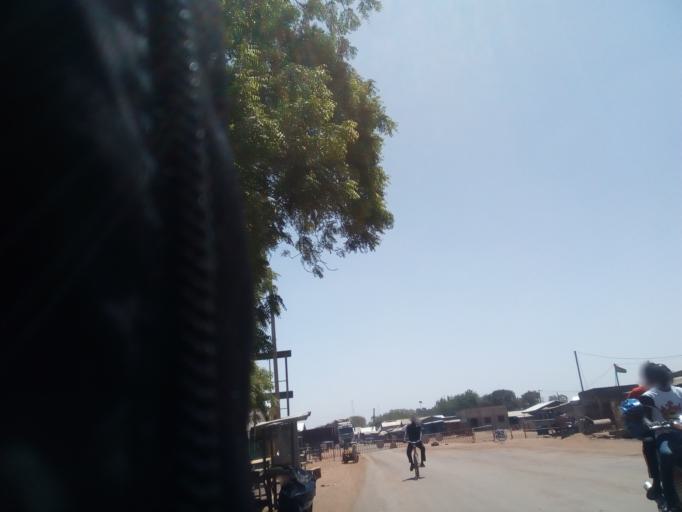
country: GH
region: Upper East
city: Navrongo
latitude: 10.9987
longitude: -1.1154
